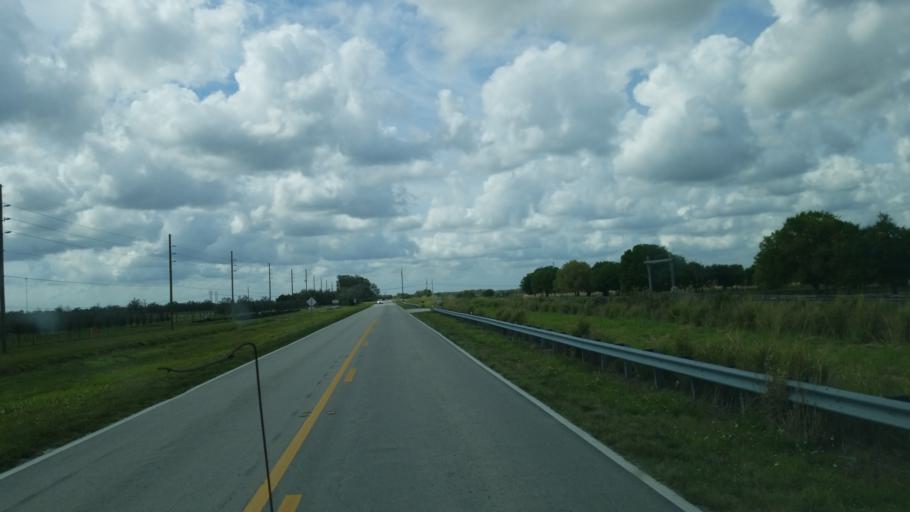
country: US
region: Florida
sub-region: Saint Lucie County
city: Lakewood Park
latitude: 27.4477
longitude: -80.5311
